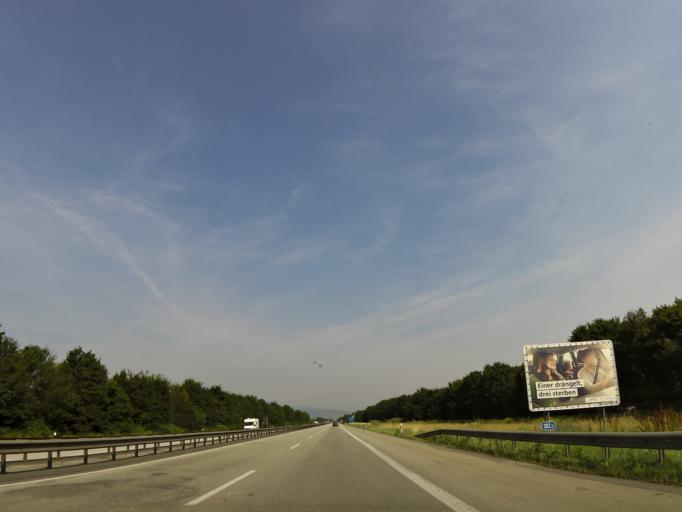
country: DE
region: Rheinland-Pfalz
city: Zotzenheim
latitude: 49.8674
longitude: 7.9634
